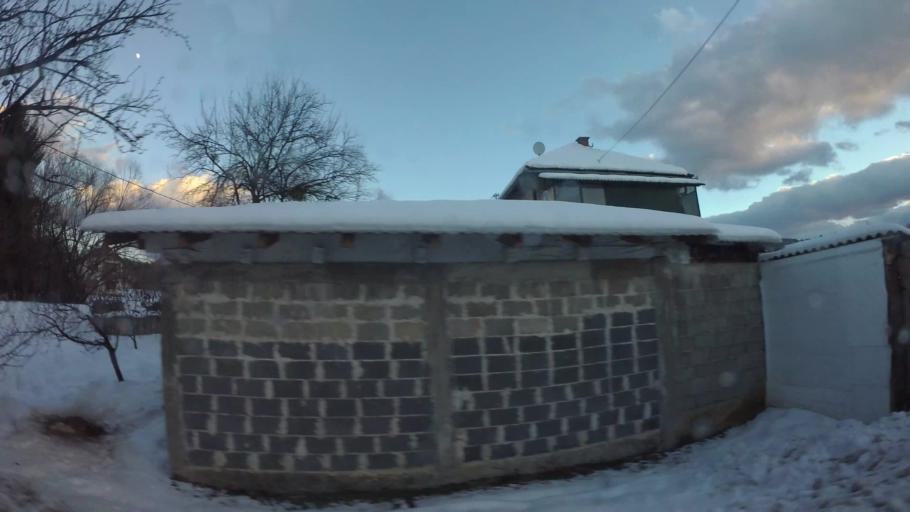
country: BA
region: Federation of Bosnia and Herzegovina
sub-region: Kanton Sarajevo
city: Sarajevo
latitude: 43.8075
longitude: 18.3761
